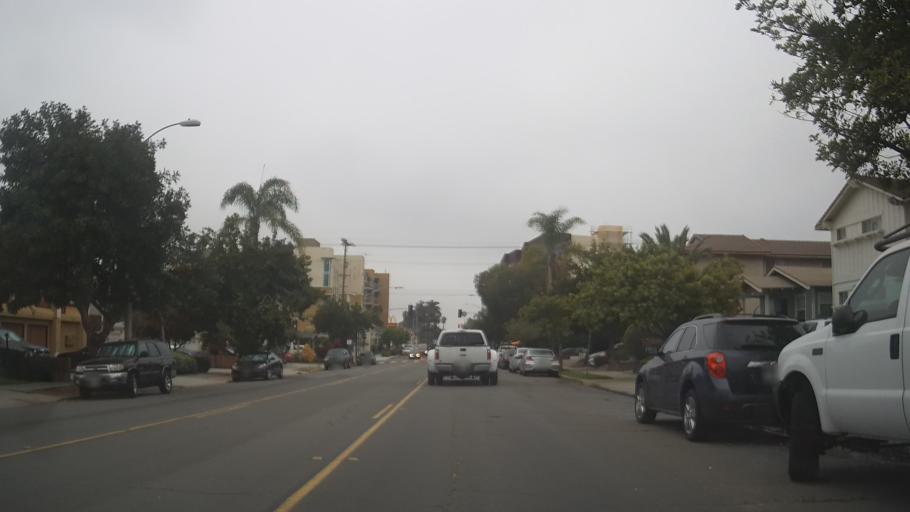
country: US
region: California
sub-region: San Diego County
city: San Diego
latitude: 32.7531
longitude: -117.1388
